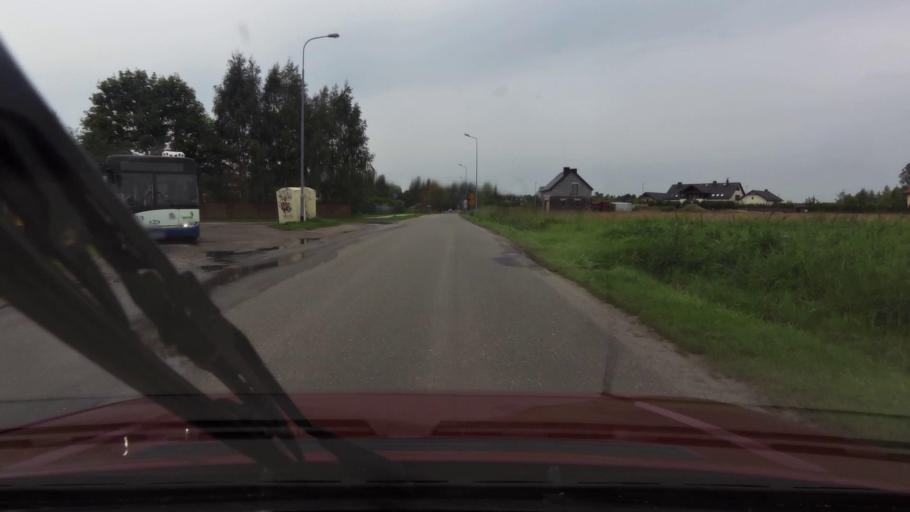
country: PL
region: West Pomeranian Voivodeship
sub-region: Powiat kolobrzeski
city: Kolobrzeg
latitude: 54.1529
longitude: 15.5401
